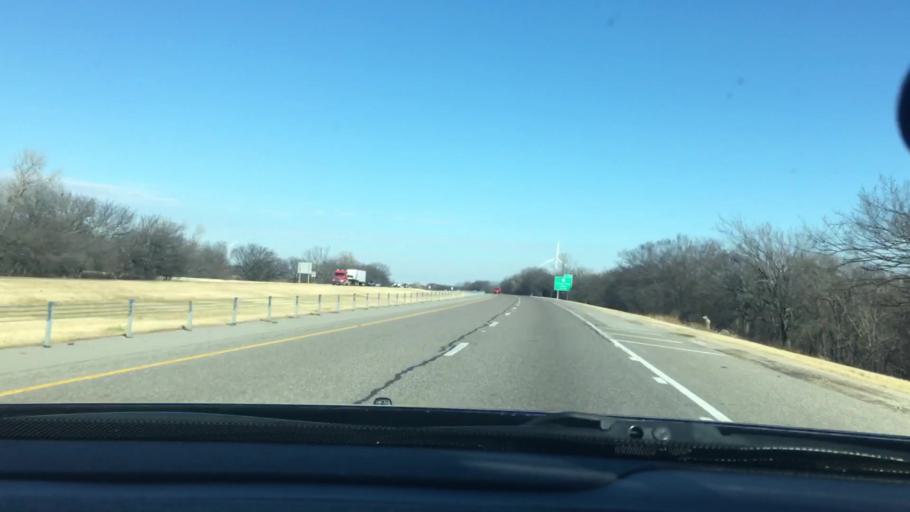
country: US
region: Oklahoma
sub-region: Murray County
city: Davis
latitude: 34.3822
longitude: -97.1424
